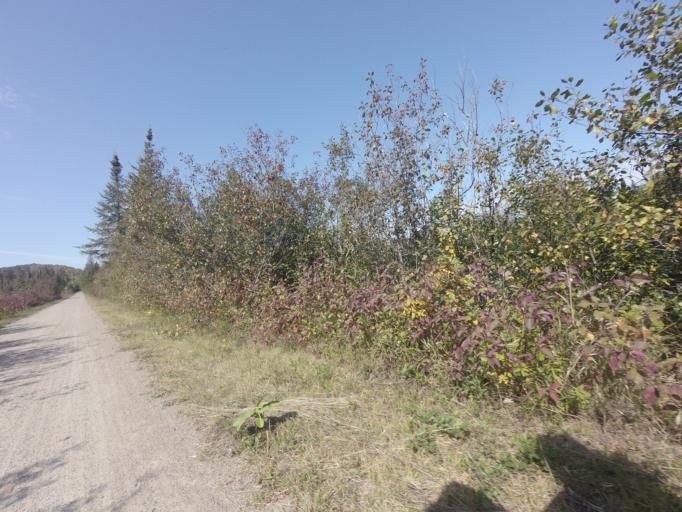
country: CA
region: Quebec
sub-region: Laurentides
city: Sainte-Agathe-des-Monts
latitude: 46.0789
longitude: -74.3213
